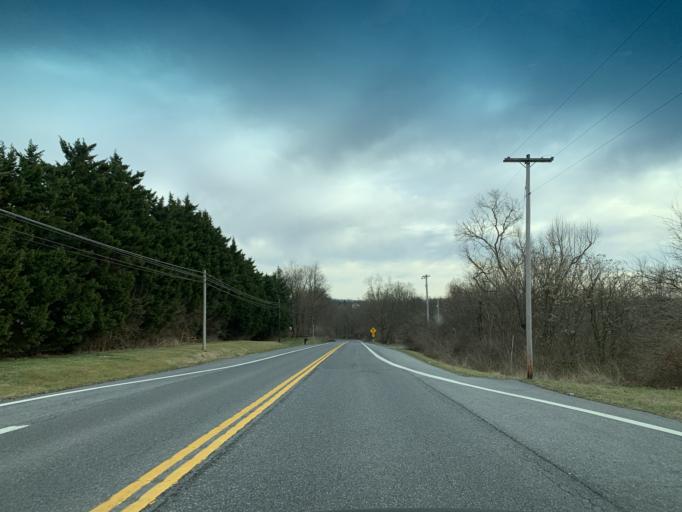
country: US
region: Maryland
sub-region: Washington County
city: Robinwood
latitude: 39.5749
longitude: -77.6915
